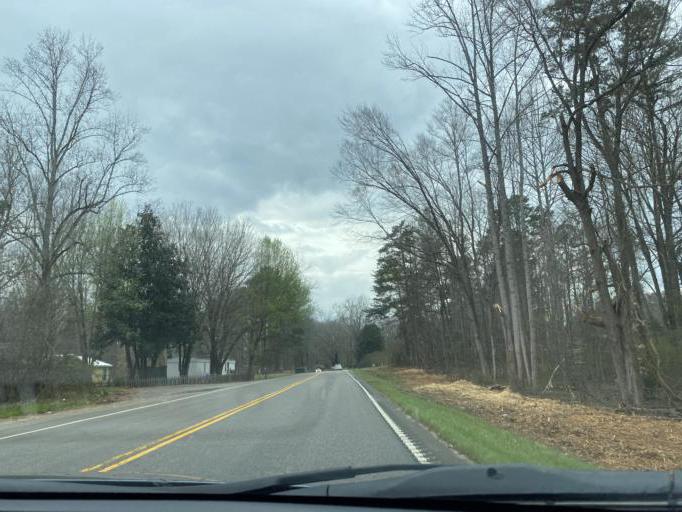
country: US
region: South Carolina
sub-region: Spartanburg County
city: Cowpens
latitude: 35.0164
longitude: -81.7285
